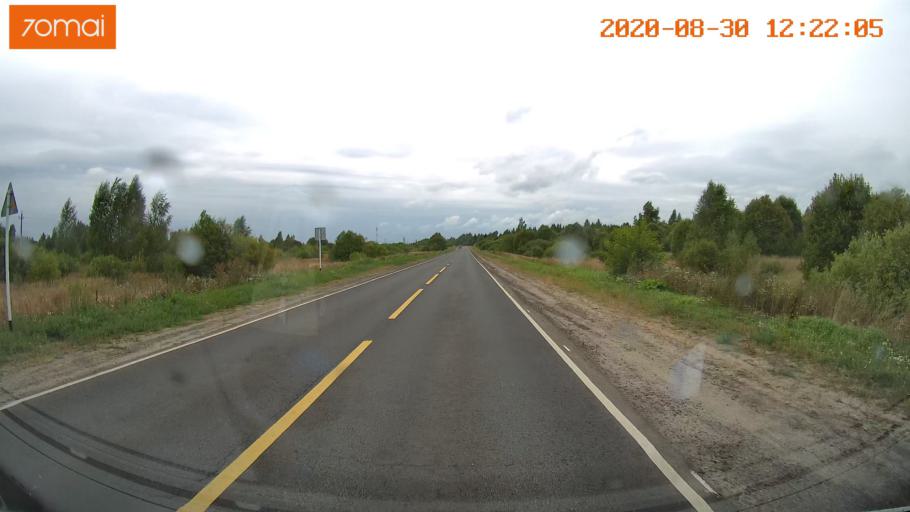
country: RU
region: Ivanovo
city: Yur'yevets
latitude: 57.3281
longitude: 42.8595
